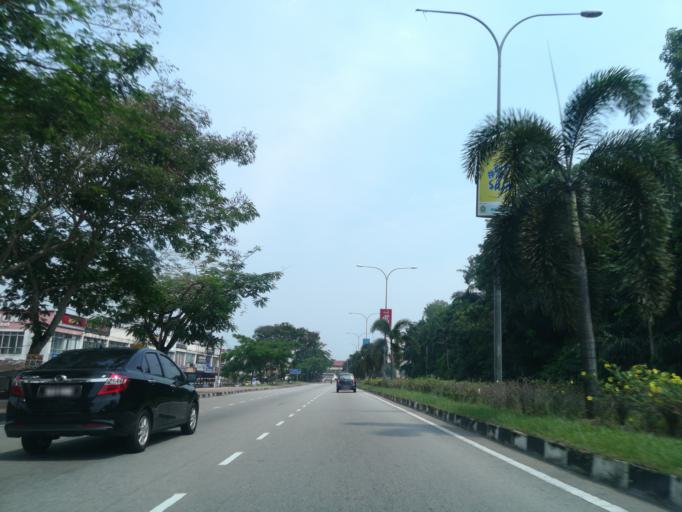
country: MY
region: Kedah
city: Kulim
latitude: 5.4127
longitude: 100.5434
